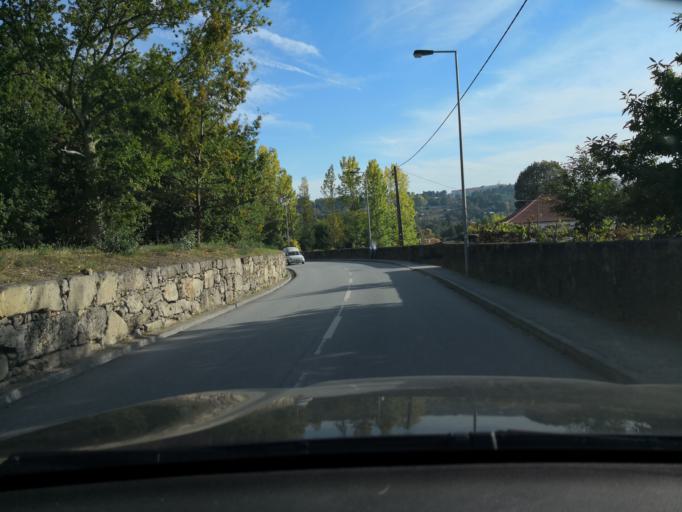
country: PT
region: Vila Real
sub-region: Vila Real
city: Vila Real
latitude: 41.3214
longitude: -7.7433
